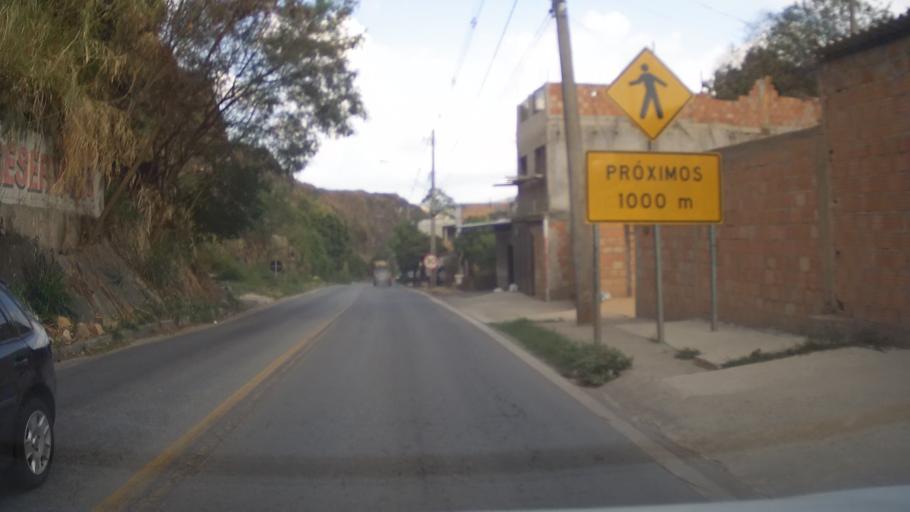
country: BR
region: Minas Gerais
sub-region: Belo Horizonte
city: Belo Horizonte
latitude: -19.8637
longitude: -43.8929
